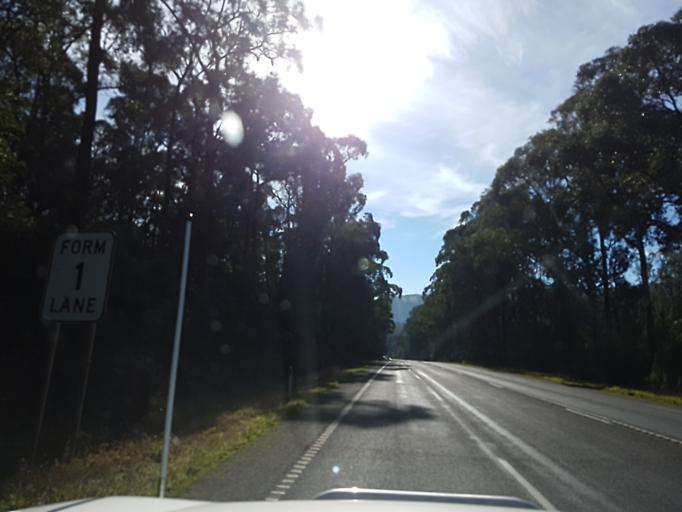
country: AU
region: Victoria
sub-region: Yarra Ranges
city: Yarra Glen
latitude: -37.5188
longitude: 145.4247
